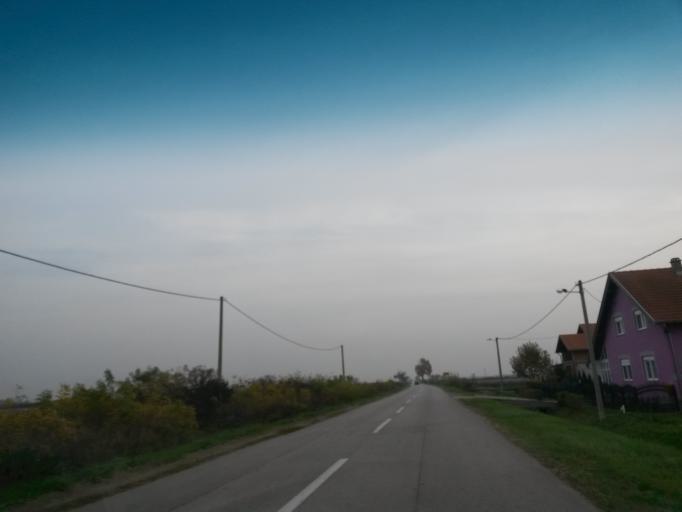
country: HR
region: Vukovarsko-Srijemska
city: Nijemci
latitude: 45.1743
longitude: 19.0143
